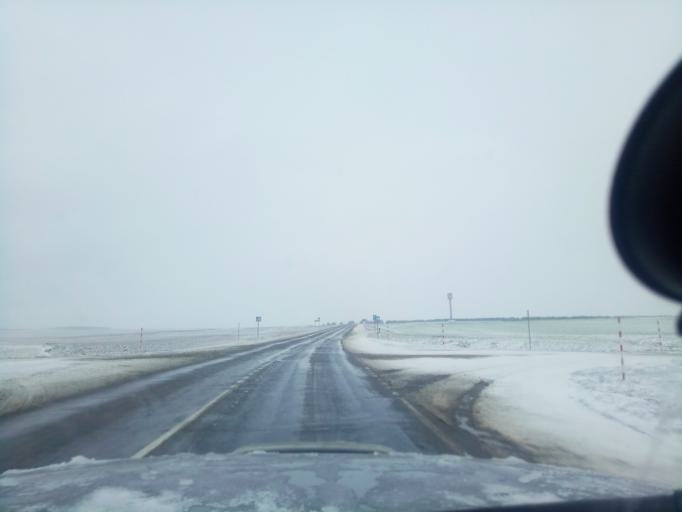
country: BY
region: Minsk
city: Haradzyeya
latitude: 53.3007
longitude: 26.5755
